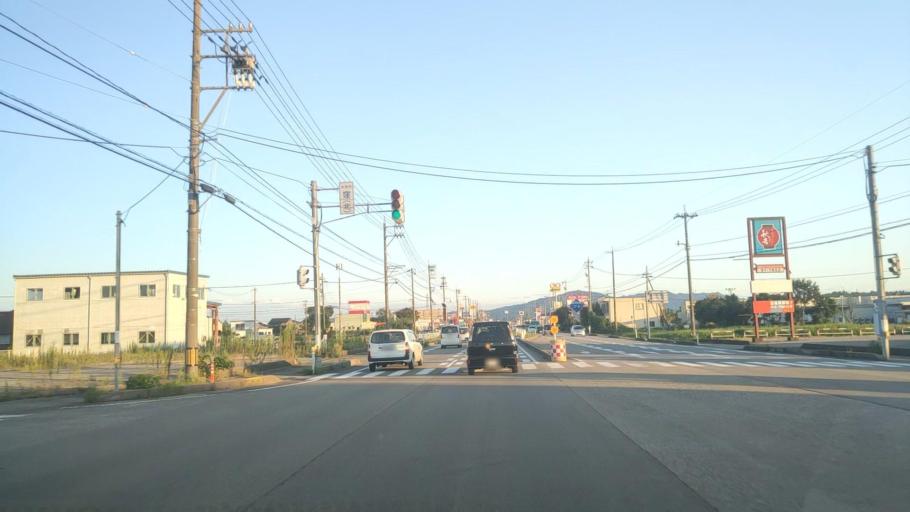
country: JP
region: Toyama
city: Himi
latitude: 36.8418
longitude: 136.9841
